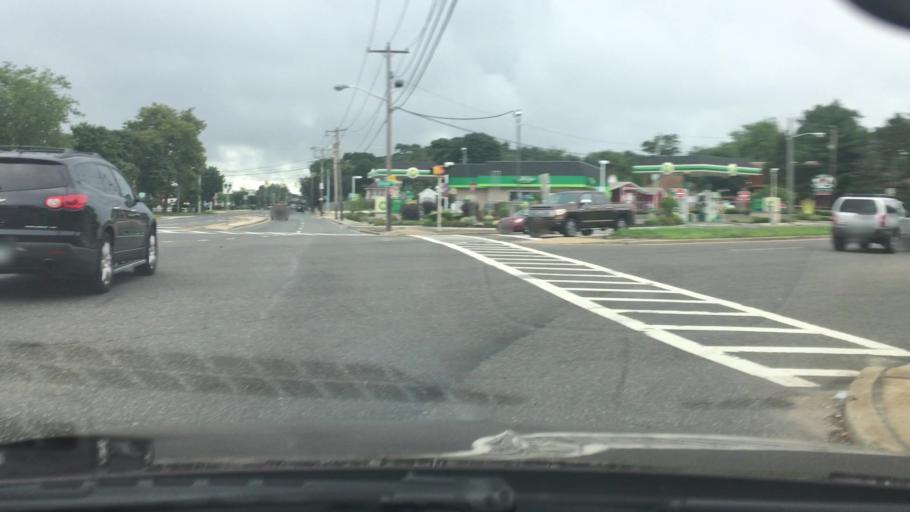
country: US
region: New York
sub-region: Suffolk County
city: North Lindenhurst
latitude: 40.7046
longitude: -73.3871
